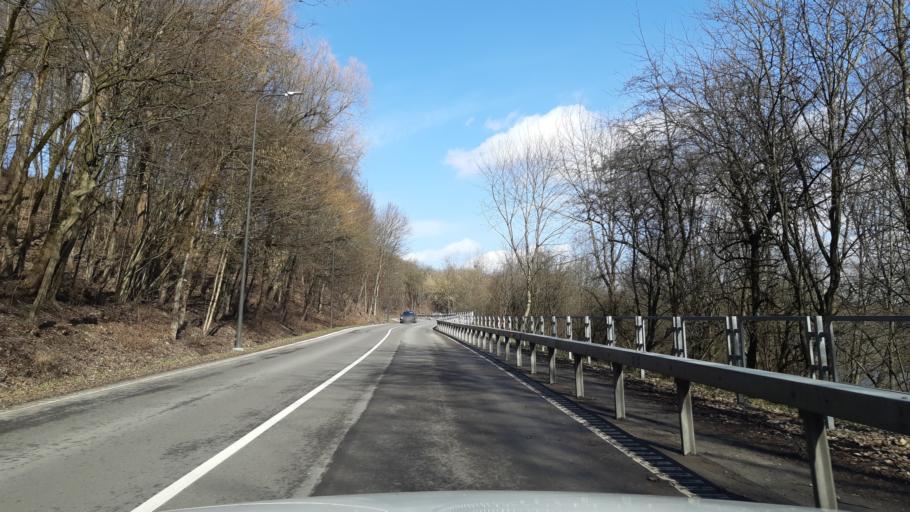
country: LT
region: Kauno apskritis
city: Dainava (Kaunas)
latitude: 54.8895
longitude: 23.9565
